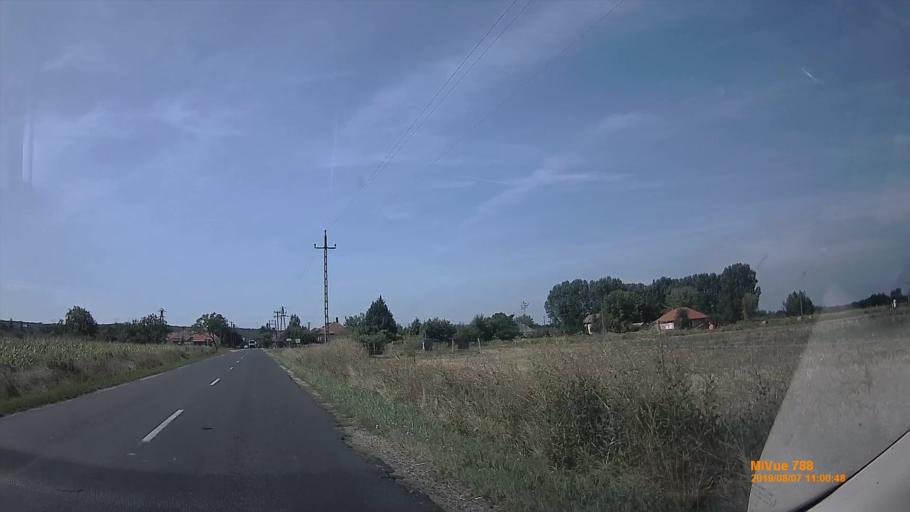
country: HU
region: Veszprem
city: Ajka
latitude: 47.0386
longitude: 17.5396
